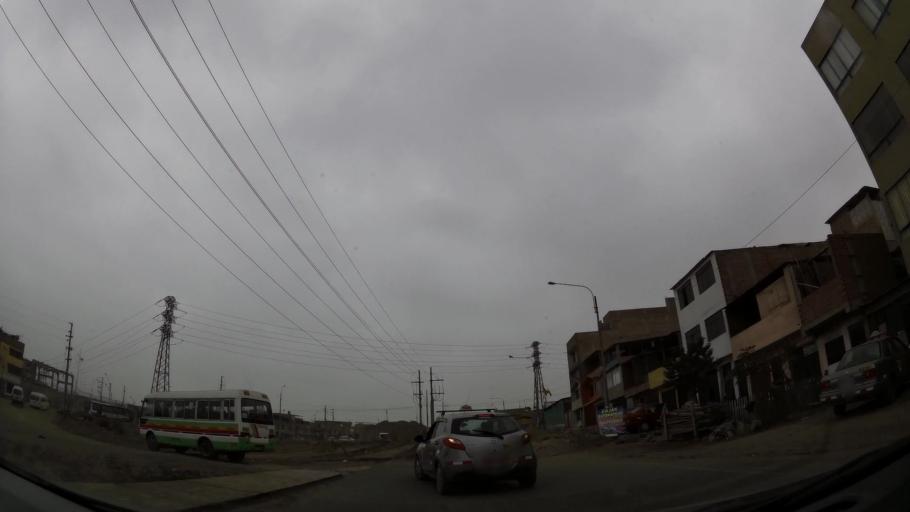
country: PE
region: Lima
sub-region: Lima
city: Surco
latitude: -12.2263
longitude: -76.9218
